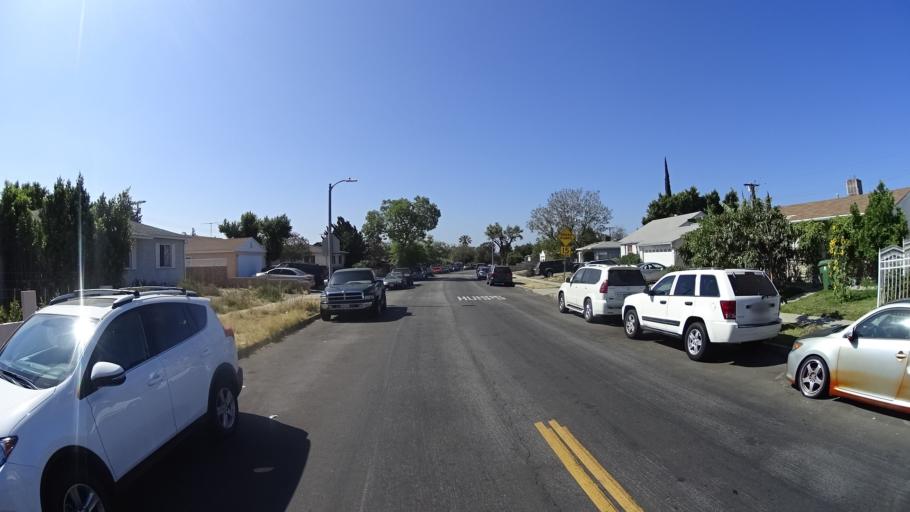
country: US
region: California
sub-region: Los Angeles County
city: Van Nuys
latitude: 34.2252
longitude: -118.4404
